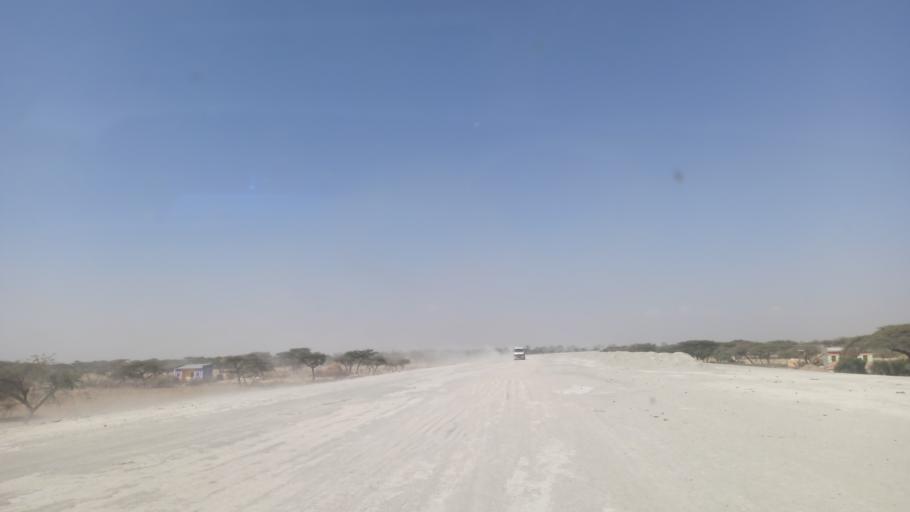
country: ET
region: Oromiya
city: Ziway
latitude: 7.6918
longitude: 38.6568
